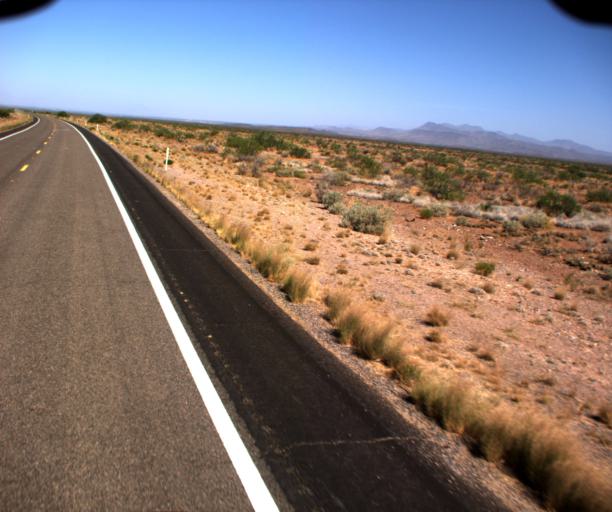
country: US
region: Arizona
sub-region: Graham County
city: Cactus Flat
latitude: 32.7645
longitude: -109.4527
